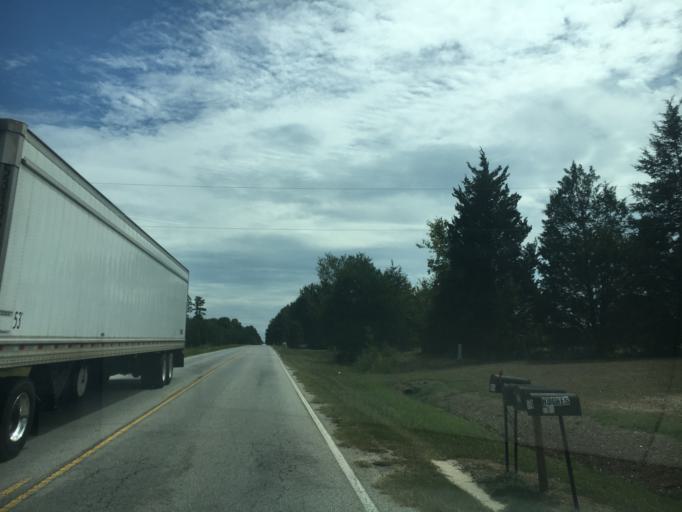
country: US
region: South Carolina
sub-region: Laurens County
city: Laurens
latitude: 34.5609
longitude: -82.0809
